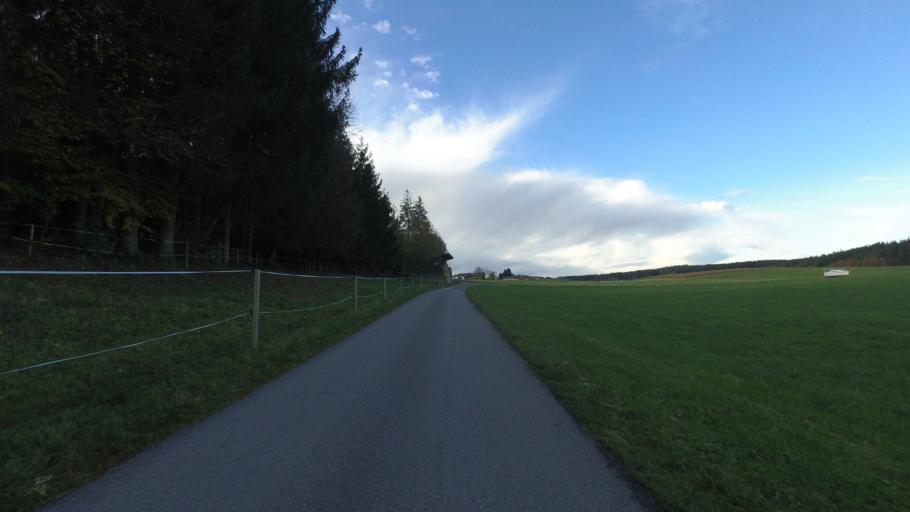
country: DE
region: Bavaria
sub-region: Upper Bavaria
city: Nussdorf
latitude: 47.9305
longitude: 12.5665
